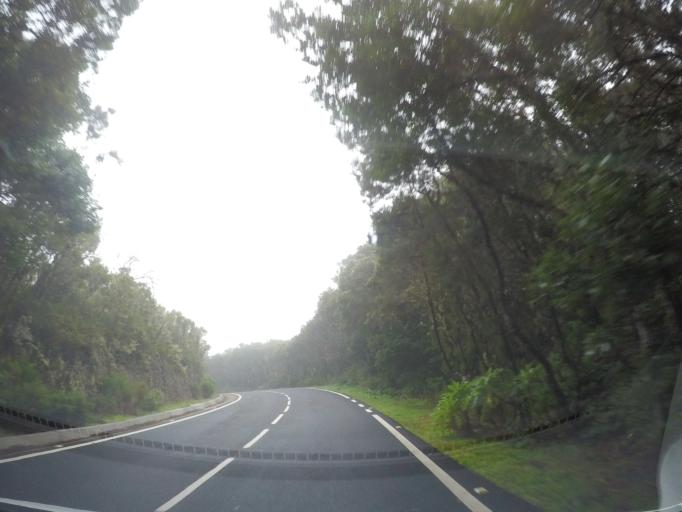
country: ES
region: Canary Islands
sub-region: Provincia de Santa Cruz de Tenerife
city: Vallehermosa
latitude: 28.1449
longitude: -17.2877
